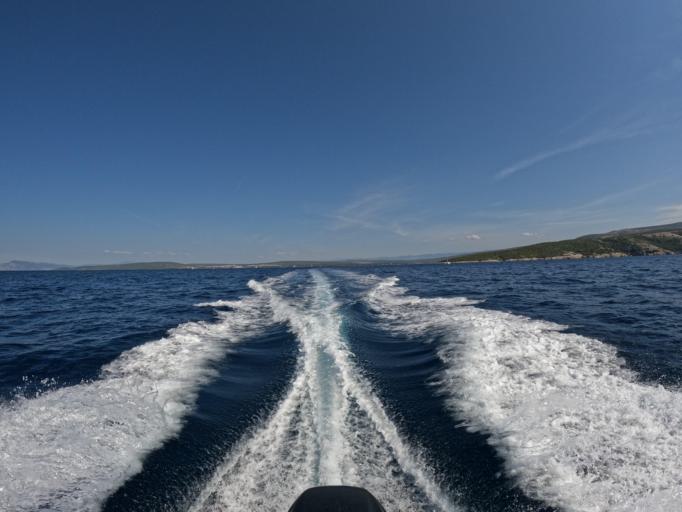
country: HR
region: Primorsko-Goranska
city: Punat
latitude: 44.9667
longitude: 14.6088
